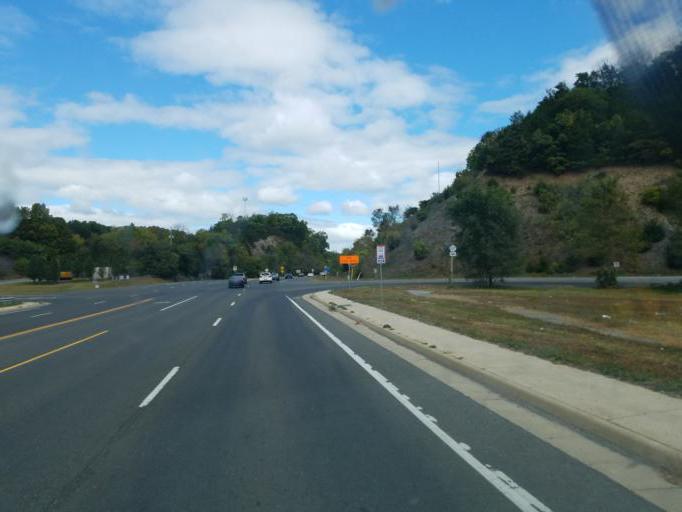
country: US
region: Virginia
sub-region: Warren County
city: Front Royal
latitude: 38.9520
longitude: -78.1997
